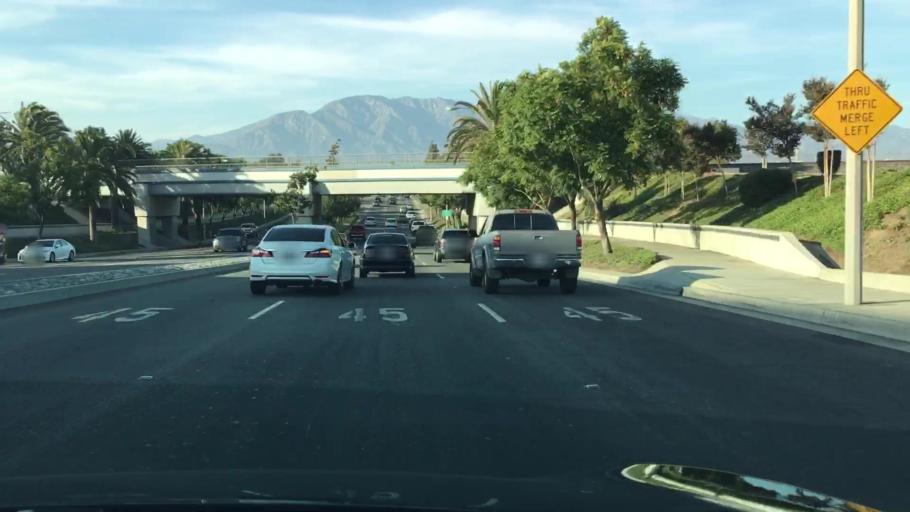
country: US
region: California
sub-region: San Bernardino County
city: Ontario
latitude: 34.0554
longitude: -117.6286
